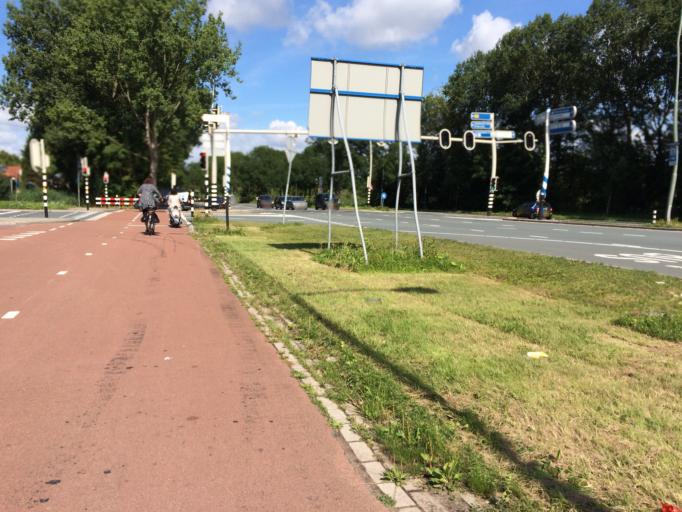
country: NL
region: South Holland
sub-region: Gemeente Dordrecht
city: Dordrecht
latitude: 51.8032
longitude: 4.6960
